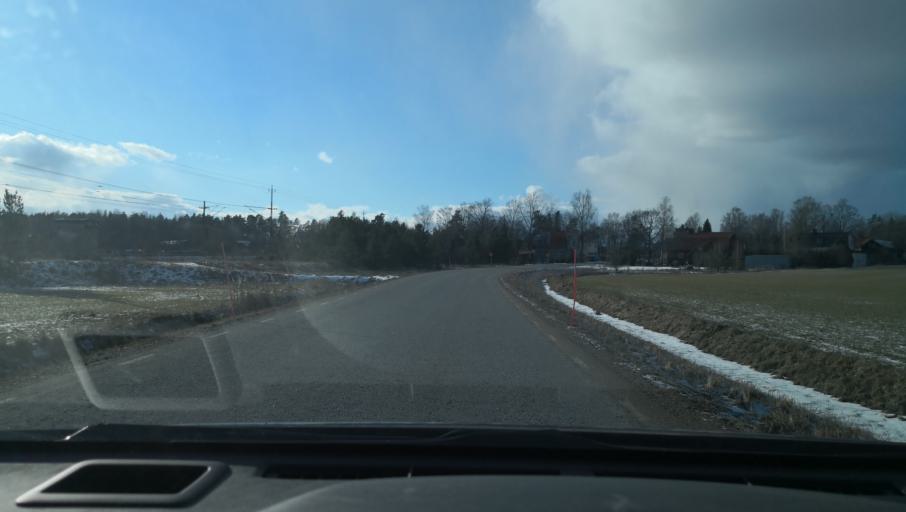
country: SE
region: Uppsala
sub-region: Enkopings Kommun
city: Hummelsta
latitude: 59.6534
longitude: 16.9483
